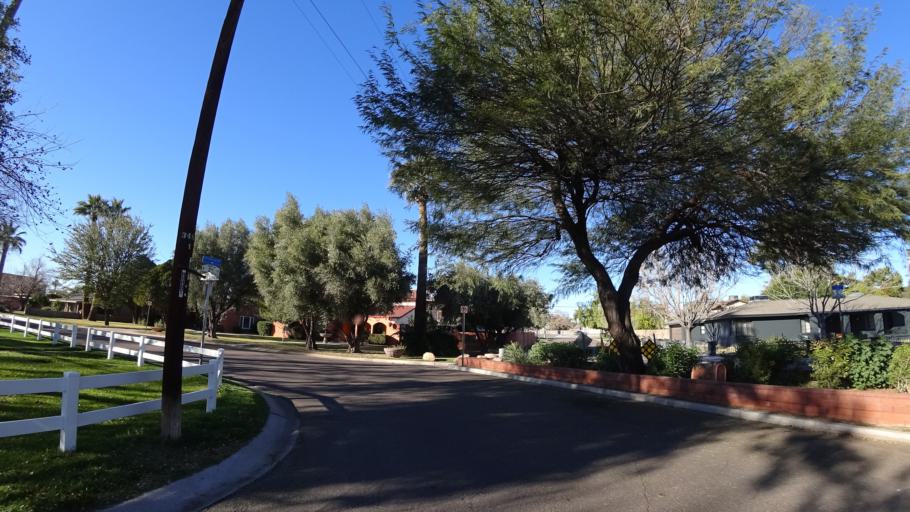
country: US
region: Arizona
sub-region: Maricopa County
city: Phoenix
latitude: 33.5137
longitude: -112.0708
